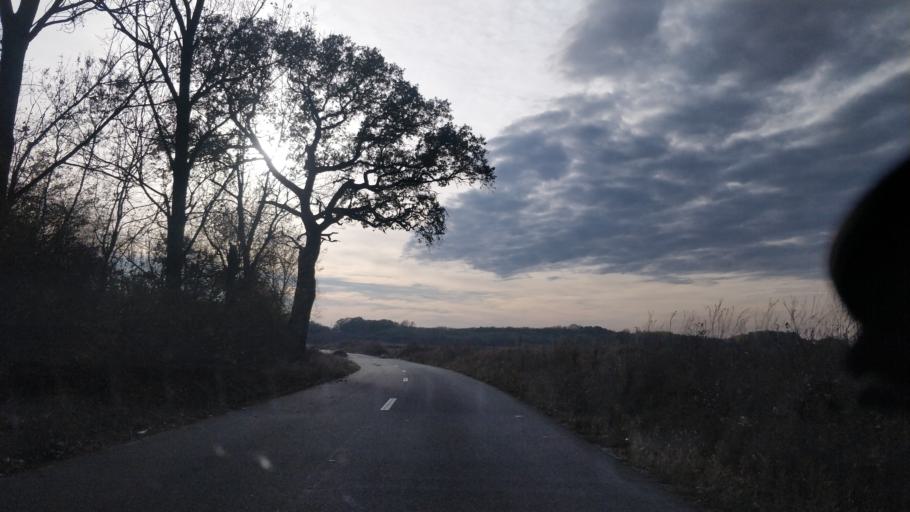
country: RO
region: Giurgiu
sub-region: Comuna Bucsani
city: Bucsani
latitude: 44.3404
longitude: 25.6660
